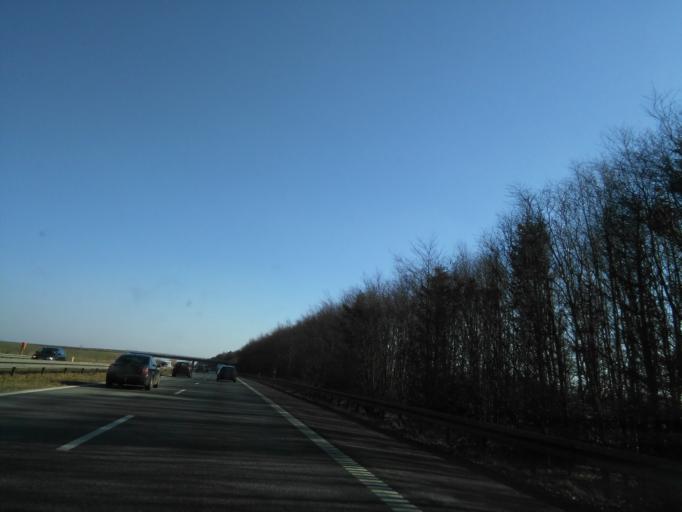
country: DK
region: South Denmark
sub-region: Nyborg Kommune
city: Ullerslev
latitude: 55.3448
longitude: 10.6240
